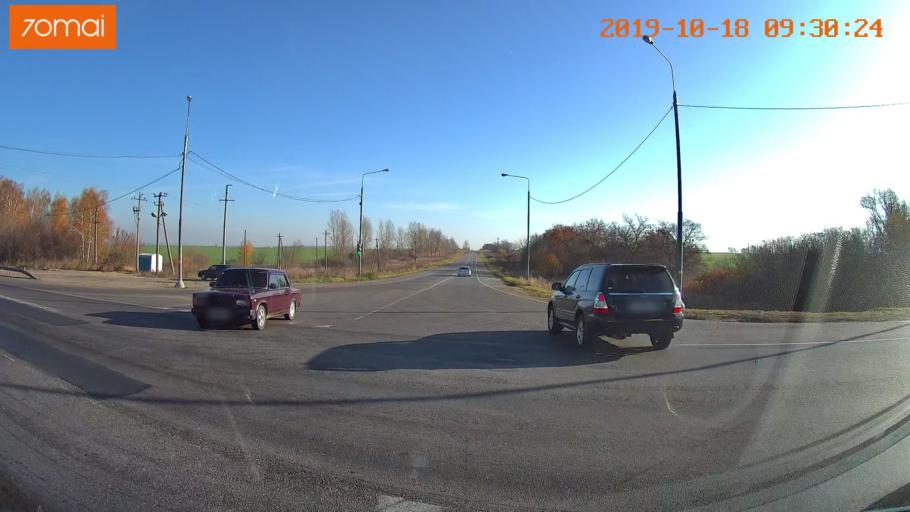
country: RU
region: Tula
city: Yefremov
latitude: 53.1390
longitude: 38.1595
